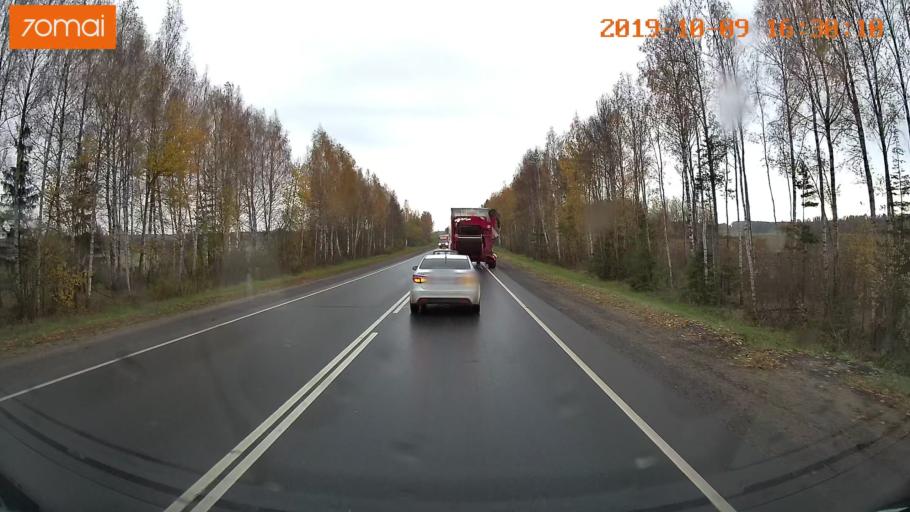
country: RU
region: Kostroma
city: Oktyabr'skiy
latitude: 57.6209
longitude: 40.9387
